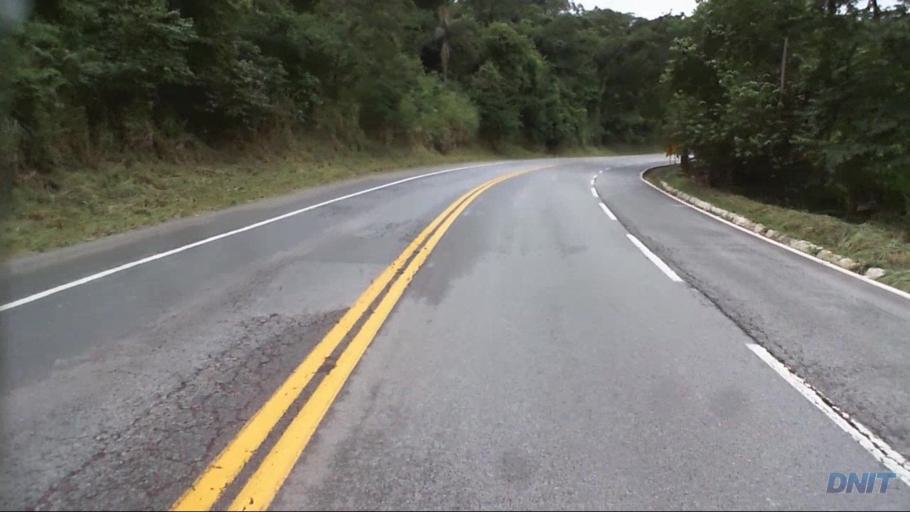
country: BR
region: Minas Gerais
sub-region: Joao Monlevade
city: Joao Monlevade
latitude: -19.8550
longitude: -43.2617
